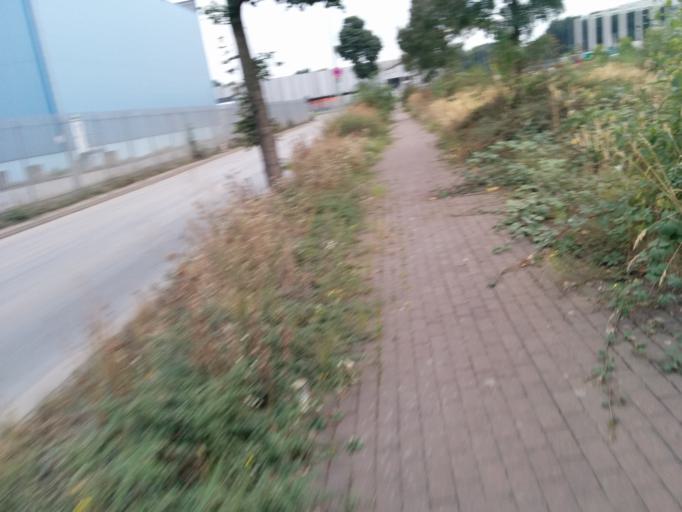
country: DE
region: North Rhine-Westphalia
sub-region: Regierungsbezirk Dusseldorf
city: Hochfeld
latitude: 51.4424
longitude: 6.7234
